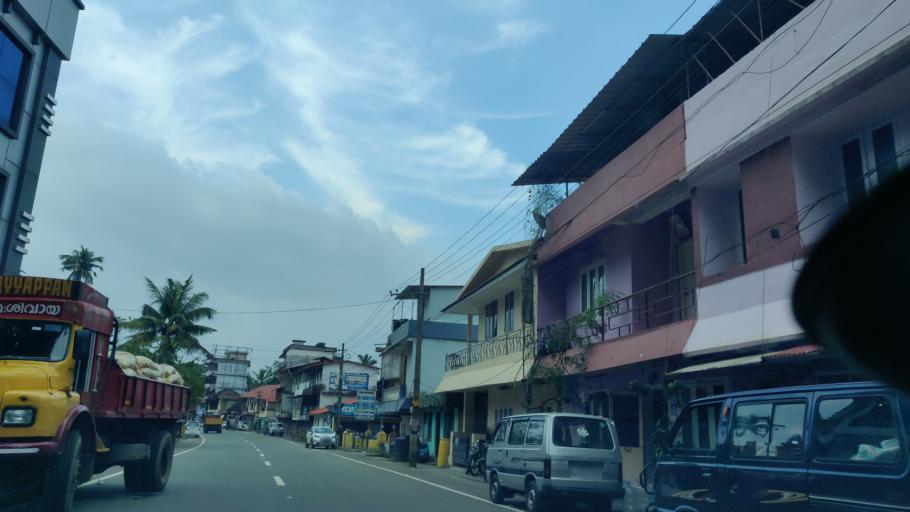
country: IN
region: Kerala
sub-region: Kottayam
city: Palackattumala
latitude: 9.8505
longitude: 76.6864
